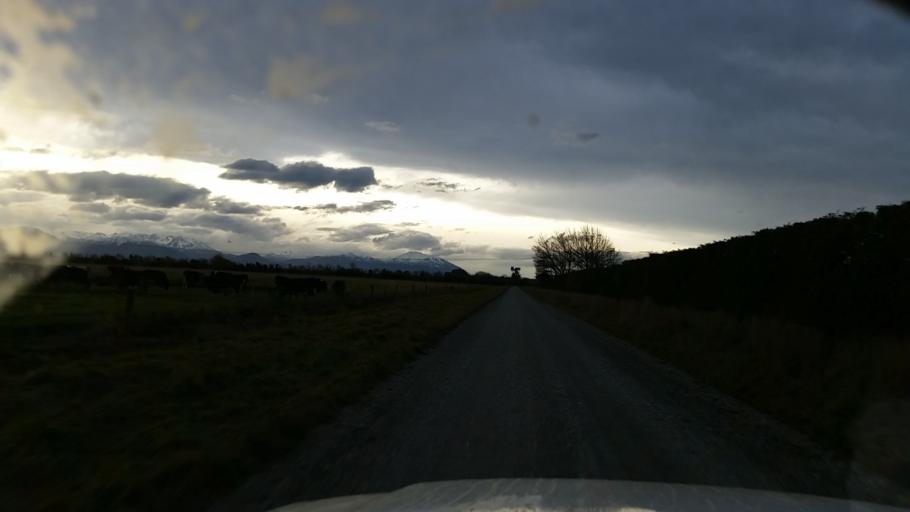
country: NZ
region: Canterbury
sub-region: Ashburton District
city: Ashburton
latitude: -43.8544
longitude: 171.6619
